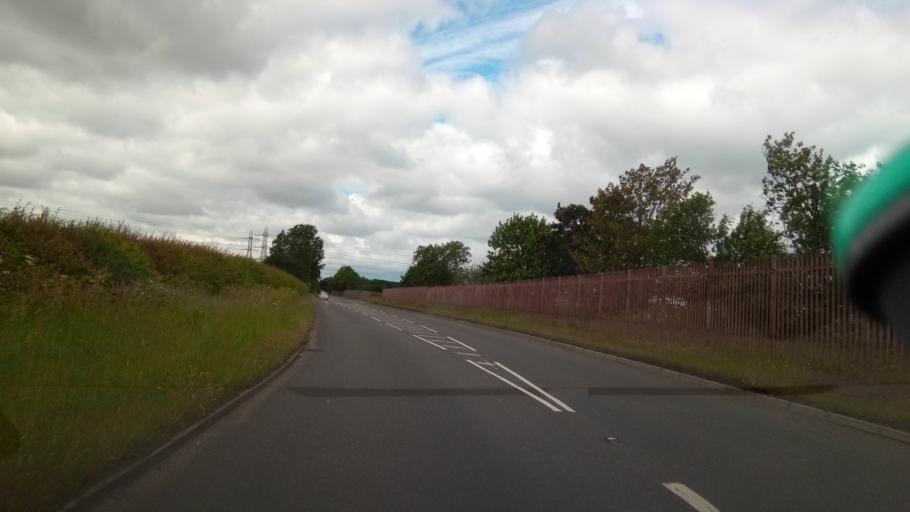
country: GB
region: England
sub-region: Derbyshire
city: Findern
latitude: 52.8544
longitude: -1.5398
